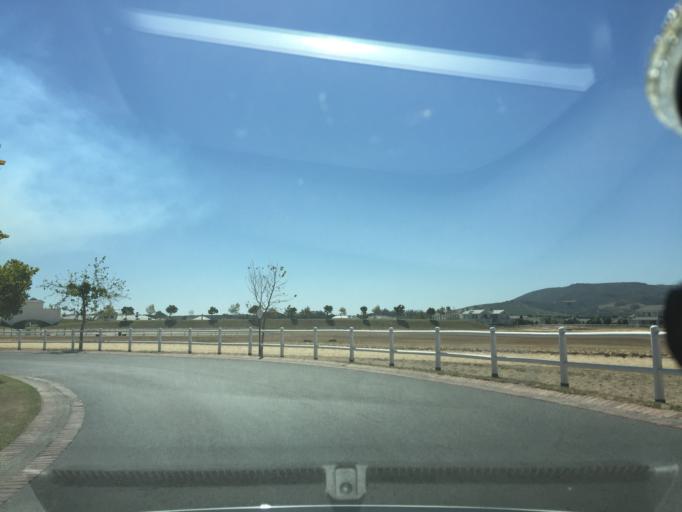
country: ZA
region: Western Cape
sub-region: Cape Winelands District Municipality
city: Paarl
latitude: -33.8051
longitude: 18.9732
